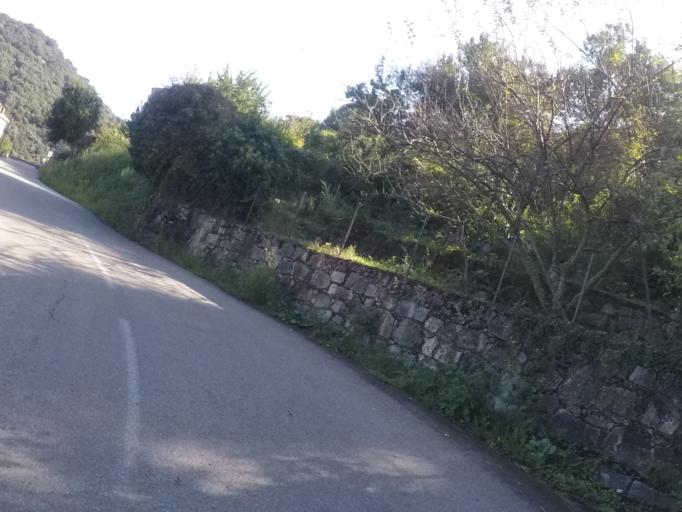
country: FR
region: Corsica
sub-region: Departement de la Corse-du-Sud
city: Olmeto
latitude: 41.7459
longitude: 8.9087
